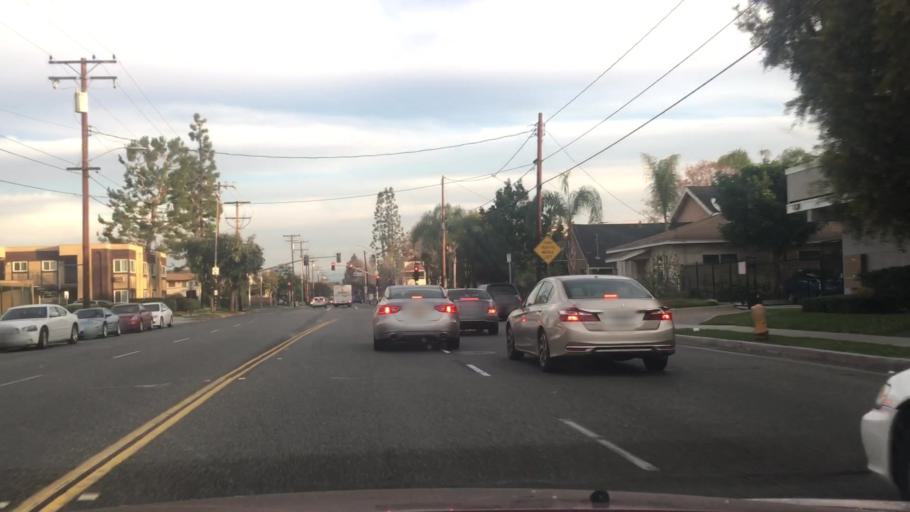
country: US
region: California
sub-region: Orange County
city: Buena Park
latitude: 33.8722
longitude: -118.0026
